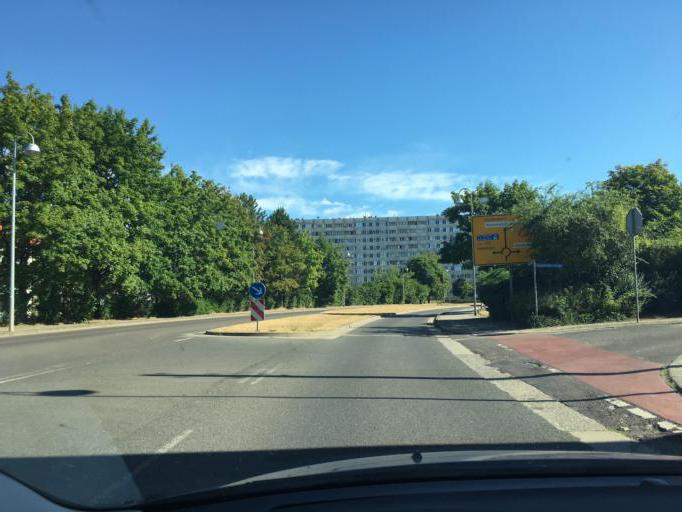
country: DE
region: Saxony-Anhalt
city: Wolmirstedt
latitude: 52.2484
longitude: 11.6221
